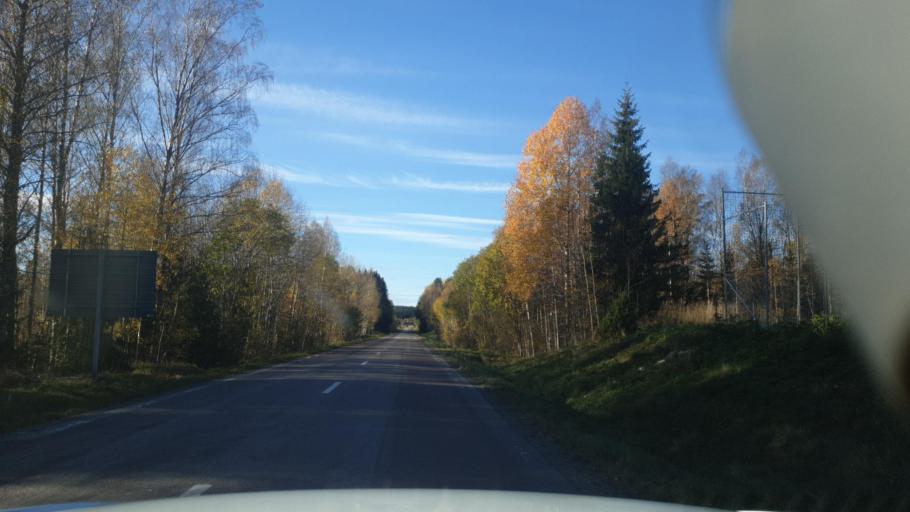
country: SE
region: Vaermland
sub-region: Arvika Kommun
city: Arvika
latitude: 59.6318
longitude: 12.8131
